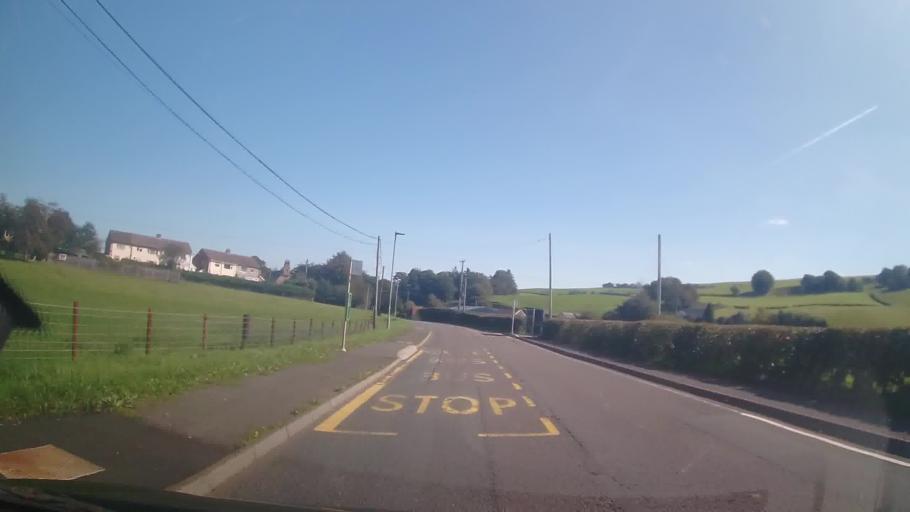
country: GB
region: Wales
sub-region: Sir Powys
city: Newtown
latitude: 52.4752
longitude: -3.3200
